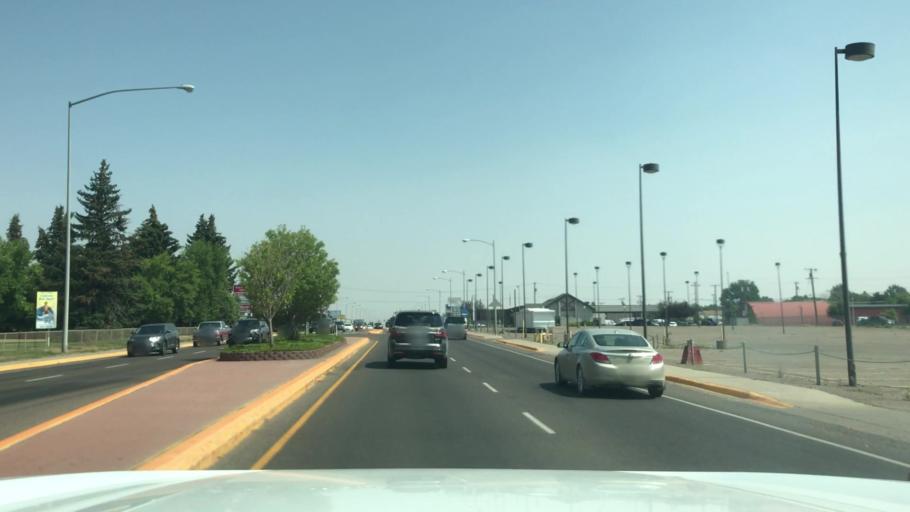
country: US
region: Montana
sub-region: Cascade County
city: Great Falls
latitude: 47.4941
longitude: -111.2602
